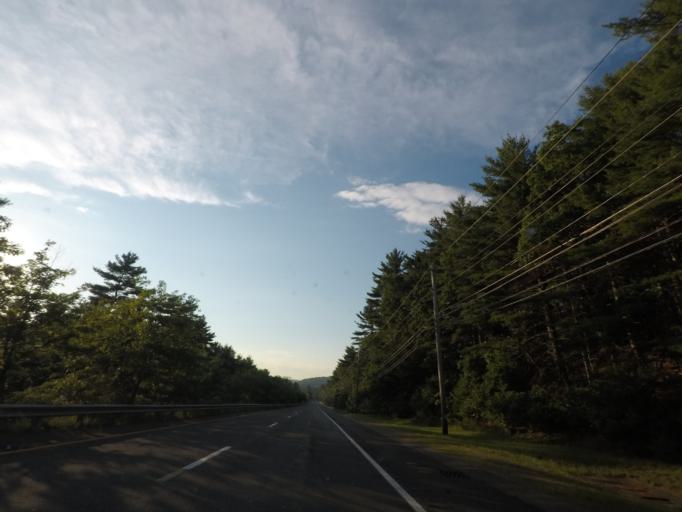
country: US
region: Massachusetts
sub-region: Hampden County
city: Brimfield
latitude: 42.1233
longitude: -72.2508
